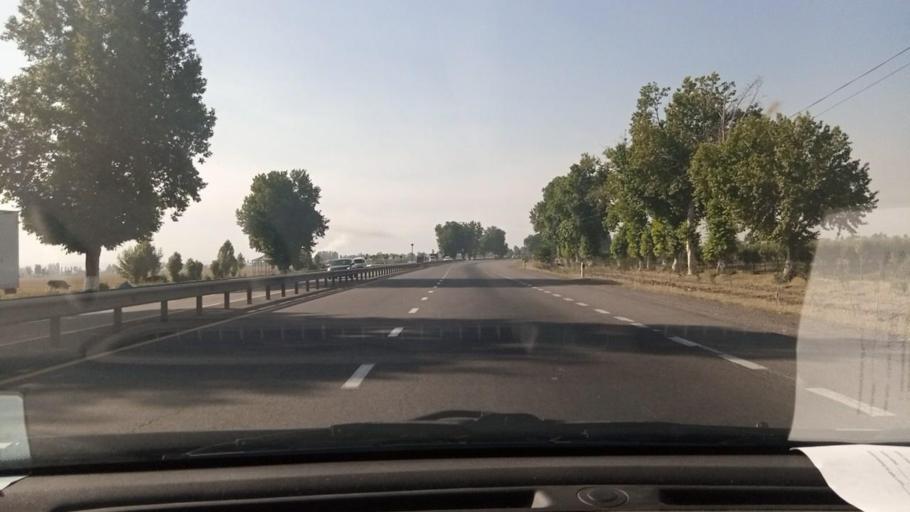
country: UZ
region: Toshkent Shahri
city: Bektemir
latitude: 41.1458
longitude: 69.4307
